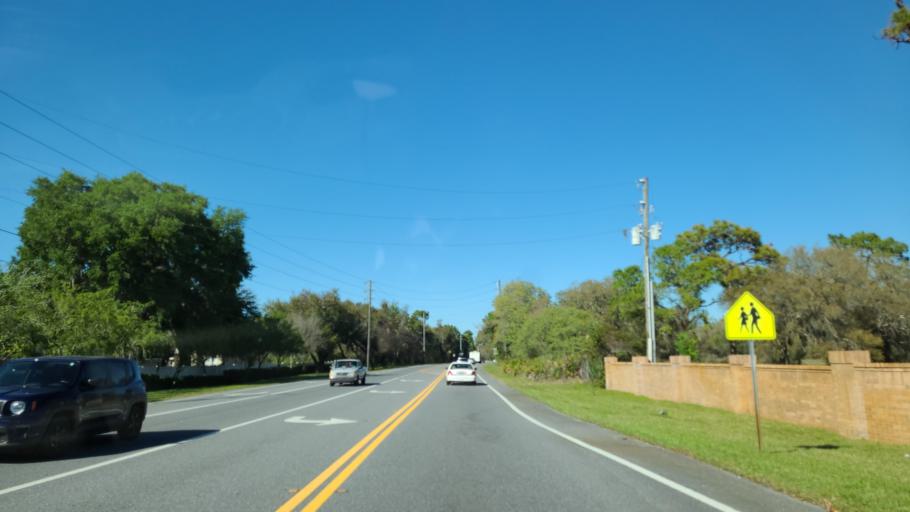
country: US
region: Florida
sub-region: Pasco County
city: Shady Hills
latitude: 28.3405
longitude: -82.5446
